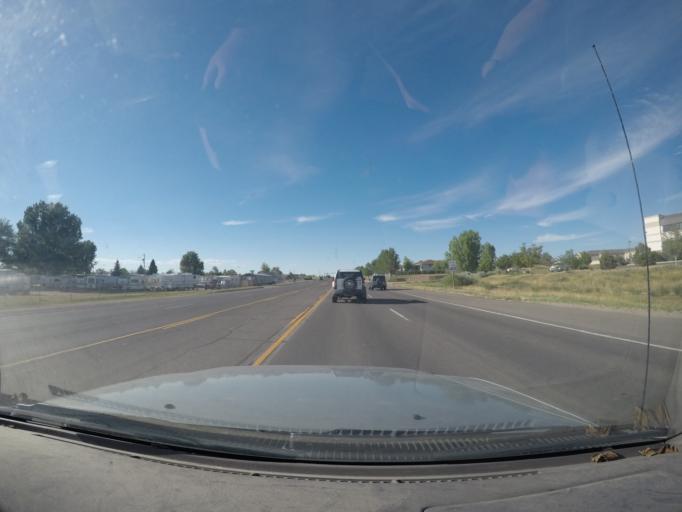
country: US
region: Wyoming
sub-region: Laramie County
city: Fox Farm-College
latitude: 41.1422
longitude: -104.7612
